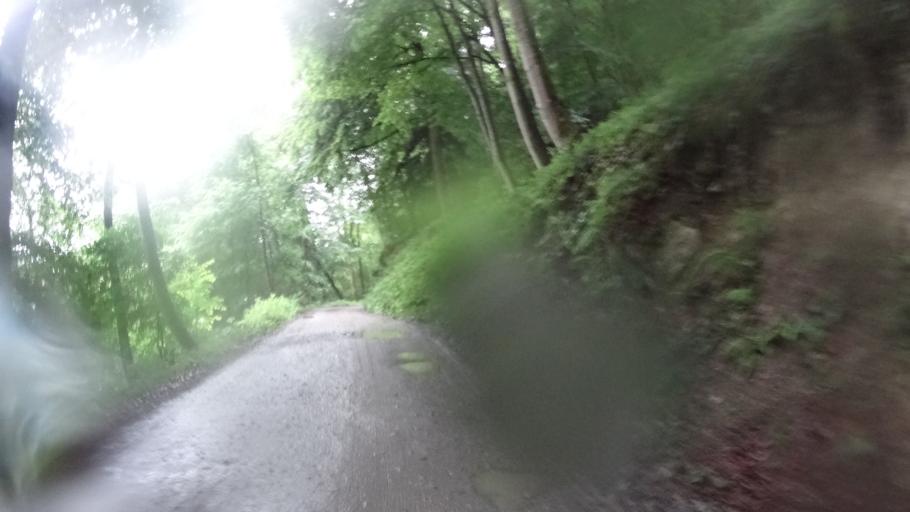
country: DE
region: Bavaria
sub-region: Lower Bavaria
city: Passau
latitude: 48.5247
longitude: 13.4445
